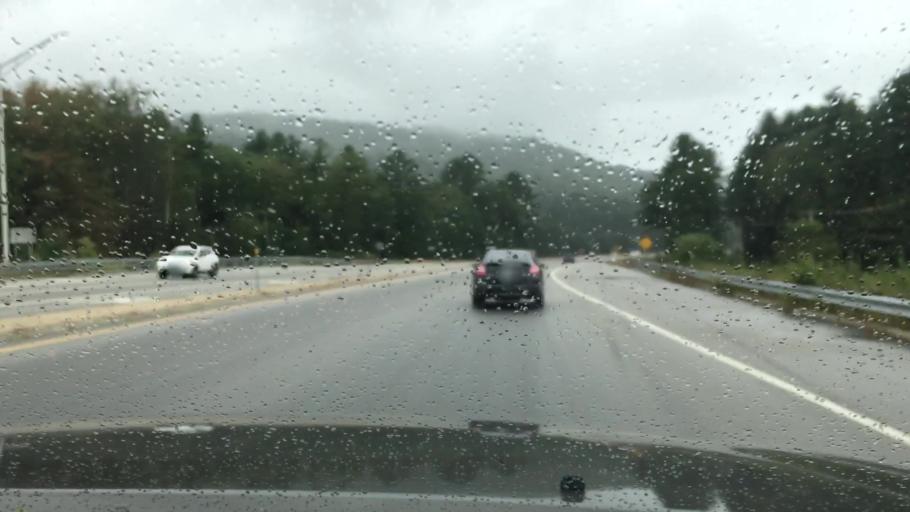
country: US
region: New Hampshire
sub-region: Cheshire County
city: Keene
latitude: 42.9237
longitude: -72.3079
